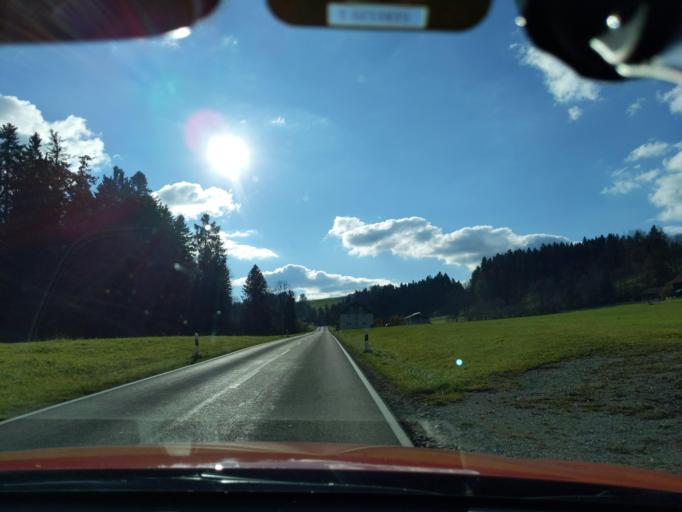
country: DE
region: Bavaria
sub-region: Swabia
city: Weiler-Simmerberg
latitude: 47.5764
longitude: 9.8953
